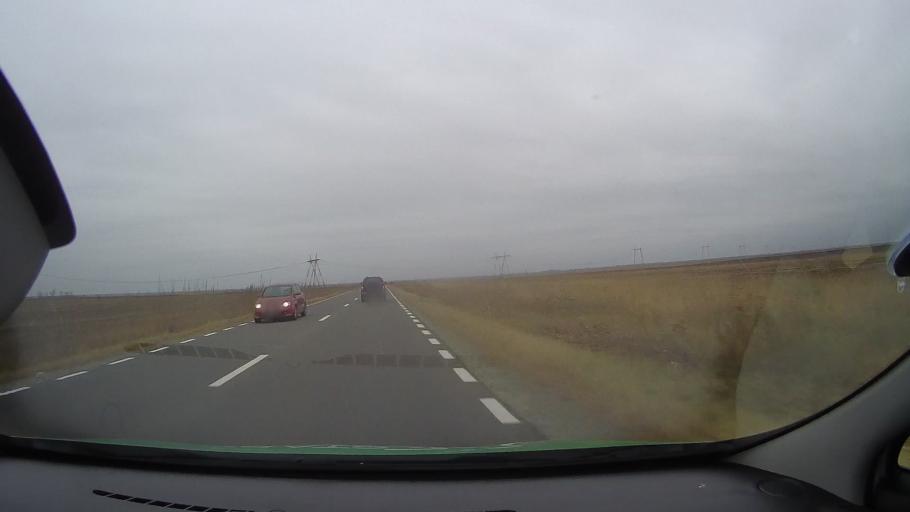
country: RO
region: Ialomita
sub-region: Comuna Gheorghe Lazar
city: Gheorghe Lazar
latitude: 44.6533
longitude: 27.4090
